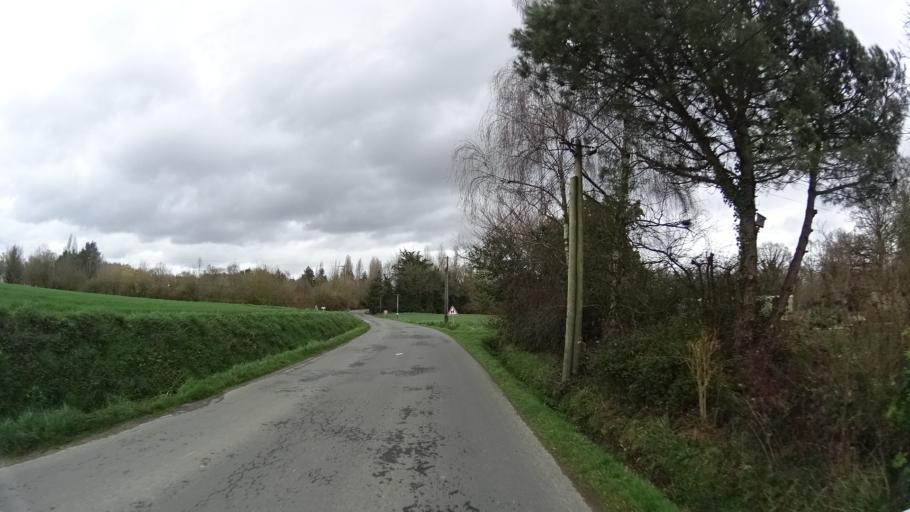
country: FR
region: Brittany
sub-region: Departement d'Ille-et-Vilaine
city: Saint-Gilles
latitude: 48.1687
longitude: -1.8296
